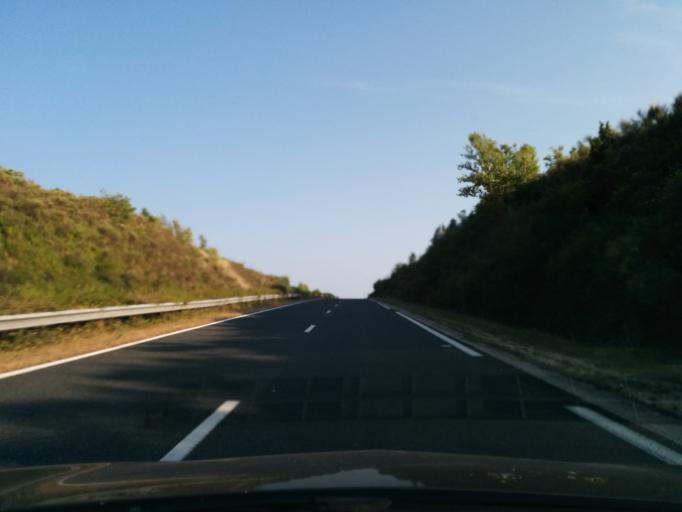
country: FR
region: Midi-Pyrenees
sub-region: Departement du Lot
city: Souillac
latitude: 44.8207
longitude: 1.4771
